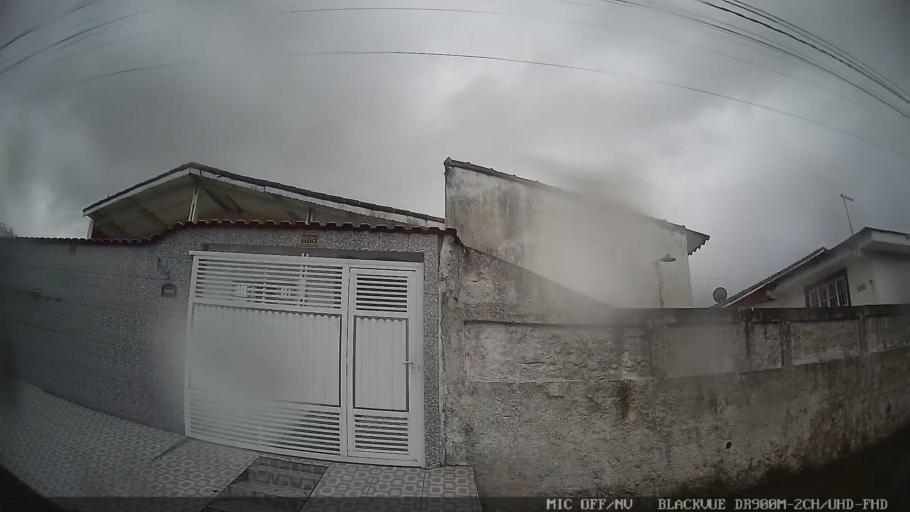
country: BR
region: Sao Paulo
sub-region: Itanhaem
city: Itanhaem
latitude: -24.1872
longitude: -46.8136
